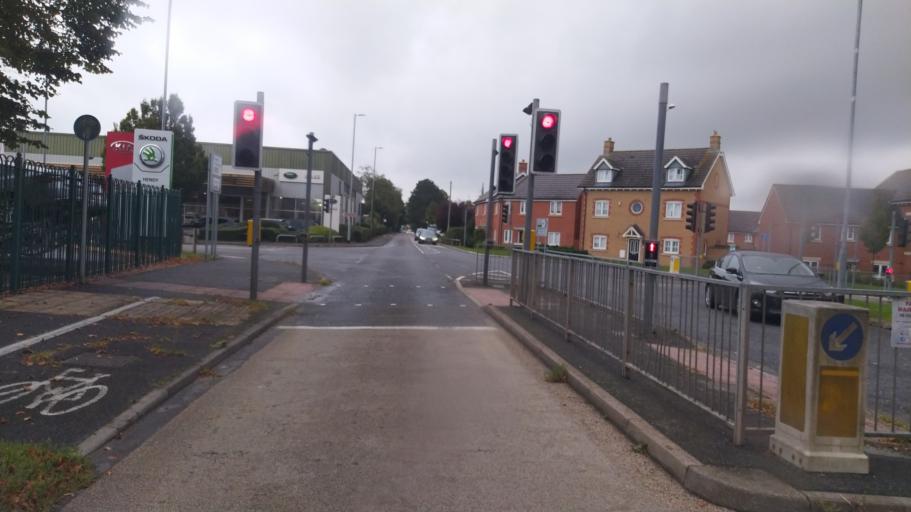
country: GB
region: England
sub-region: Wiltshire
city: Salisbury
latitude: 51.1035
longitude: -1.7803
